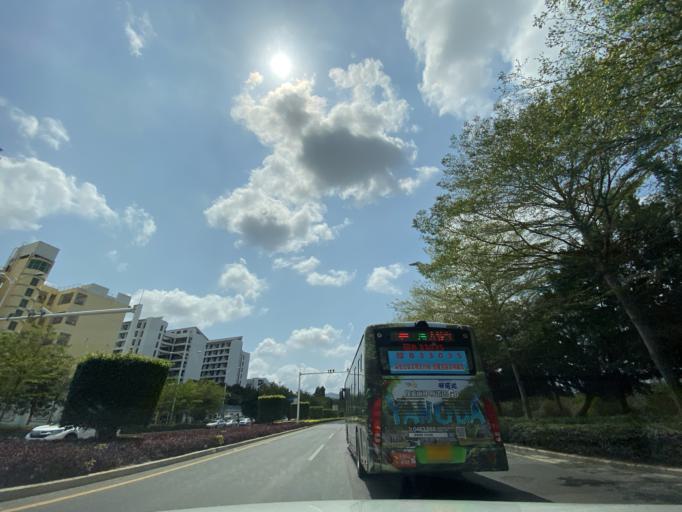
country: CN
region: Hainan
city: Tiandu
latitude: 18.3187
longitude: 109.5260
